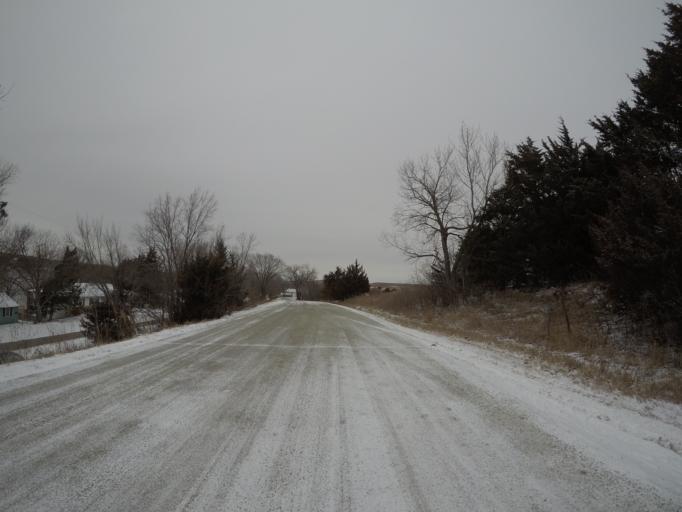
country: US
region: Kansas
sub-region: Wabaunsee County
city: Alma
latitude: 38.8598
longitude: -96.1897
